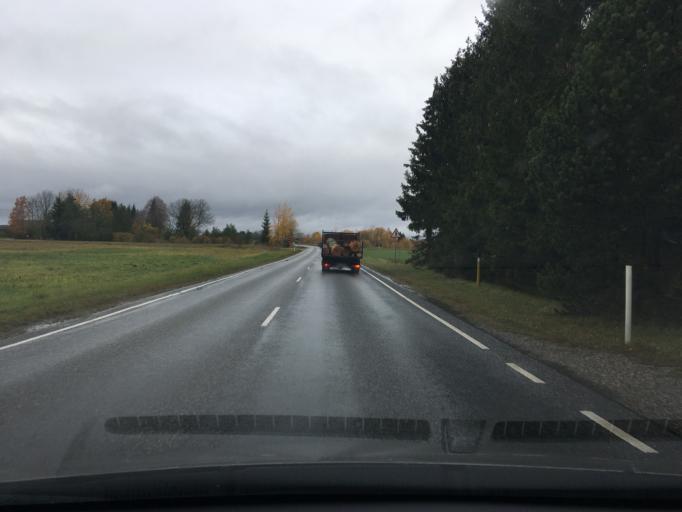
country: EE
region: Jogevamaa
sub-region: Tabivere vald
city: Tabivere
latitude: 58.4679
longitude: 26.6222
